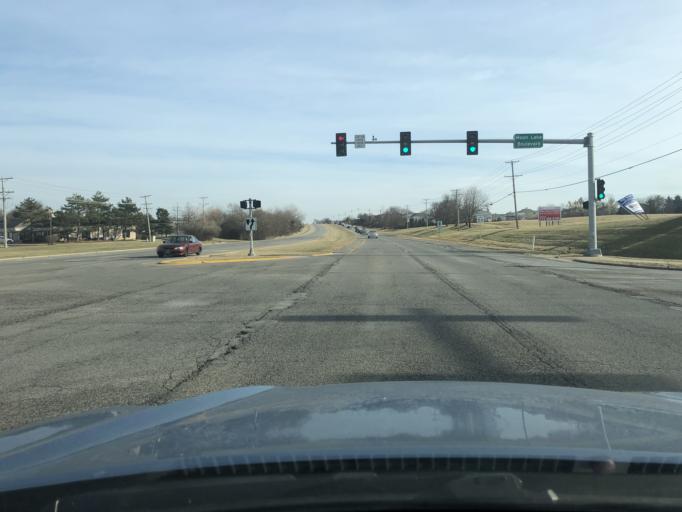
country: US
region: Illinois
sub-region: Cook County
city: South Barrington
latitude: 42.0563
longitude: -88.1356
